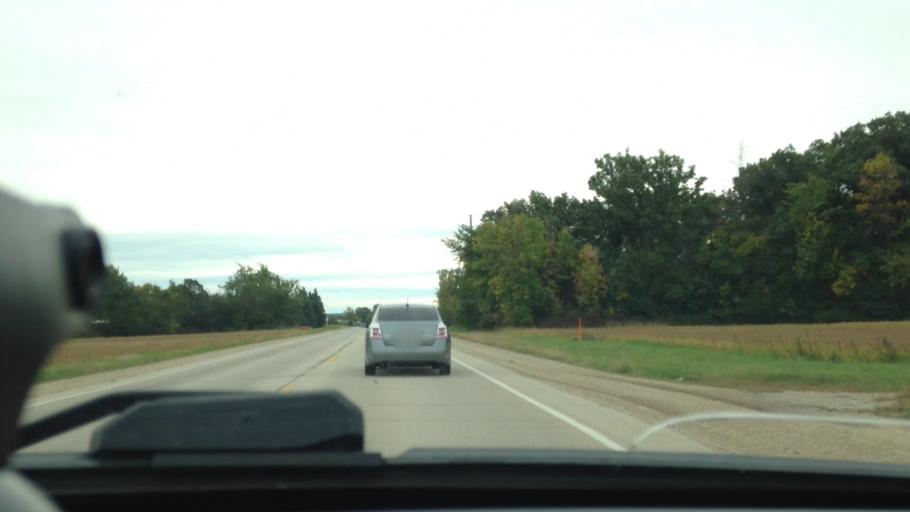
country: US
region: Wisconsin
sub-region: Fond du Lac County
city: North Fond du Lac
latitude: 43.8007
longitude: -88.4956
